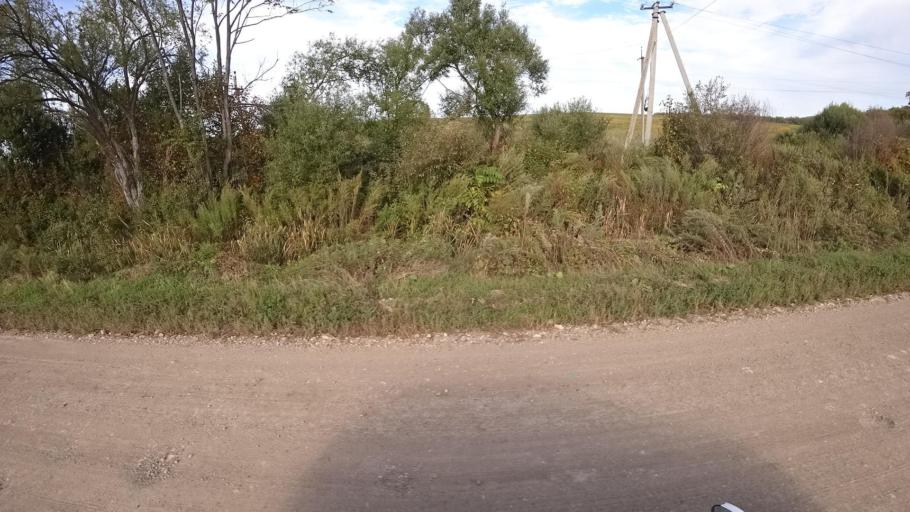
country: RU
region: Primorskiy
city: Dostoyevka
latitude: 44.3089
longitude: 133.4650
